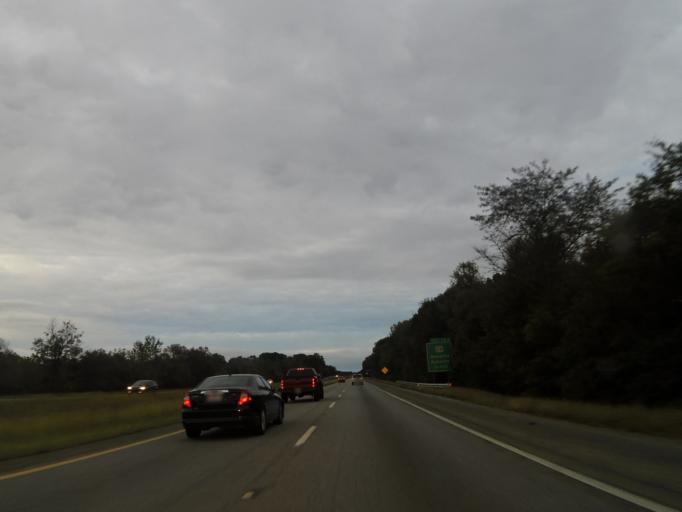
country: US
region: Alabama
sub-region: Saint Clair County
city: Ashville
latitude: 33.8570
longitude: -86.2975
